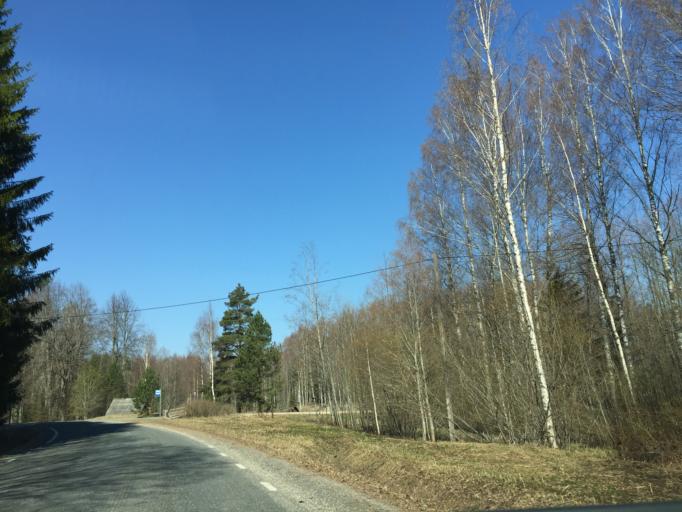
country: EE
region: Jogevamaa
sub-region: Mustvee linn
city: Mustvee
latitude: 58.5844
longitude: 26.9013
